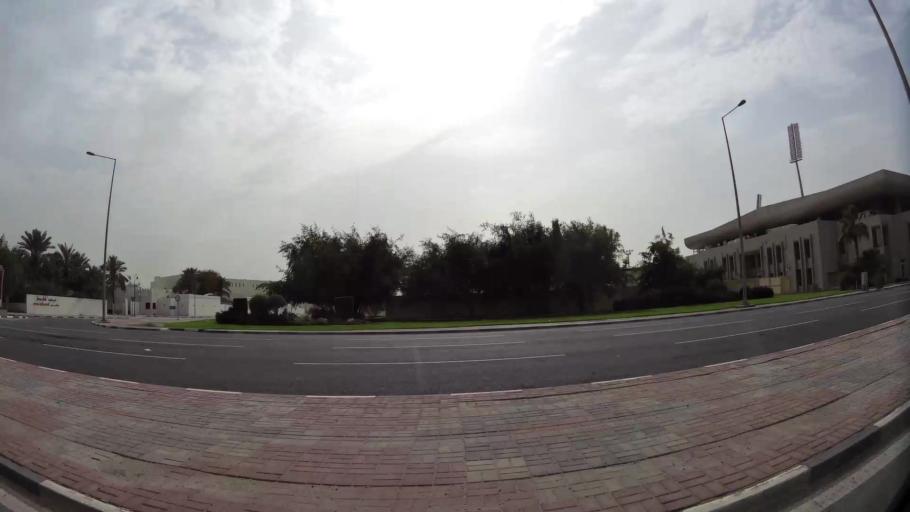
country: QA
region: Baladiyat ad Dawhah
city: Doha
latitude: 25.3161
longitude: 51.5148
